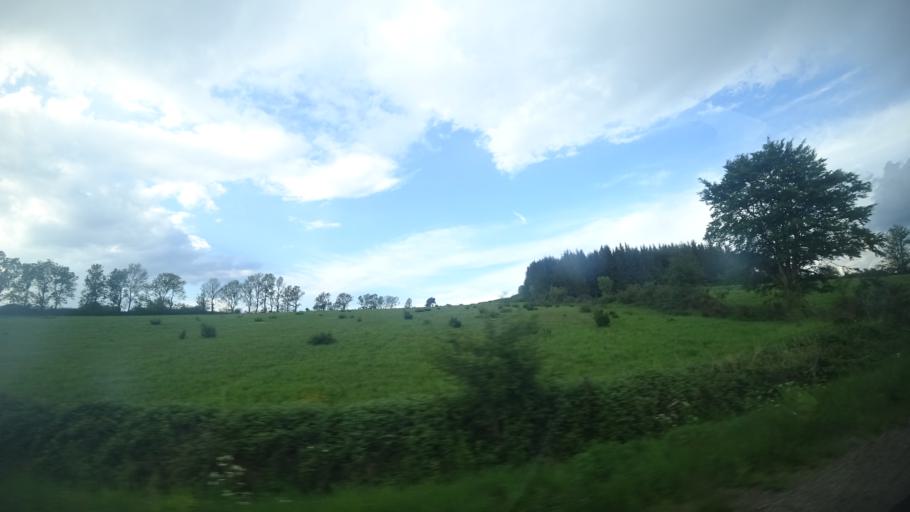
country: FR
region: Midi-Pyrenees
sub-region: Departement de l'Aveyron
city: Severac-le-Chateau
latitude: 44.2404
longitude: 2.9540
